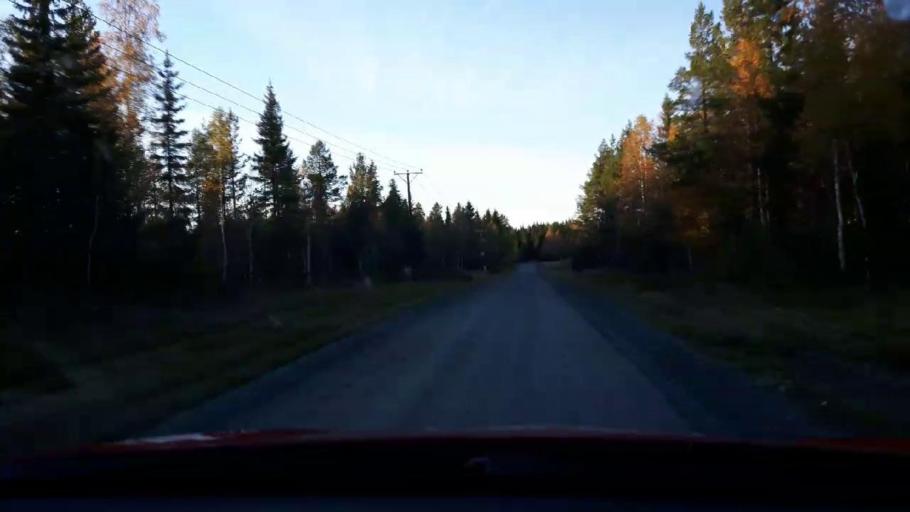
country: SE
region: Jaemtland
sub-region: Krokoms Kommun
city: Krokom
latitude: 63.4510
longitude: 14.4164
